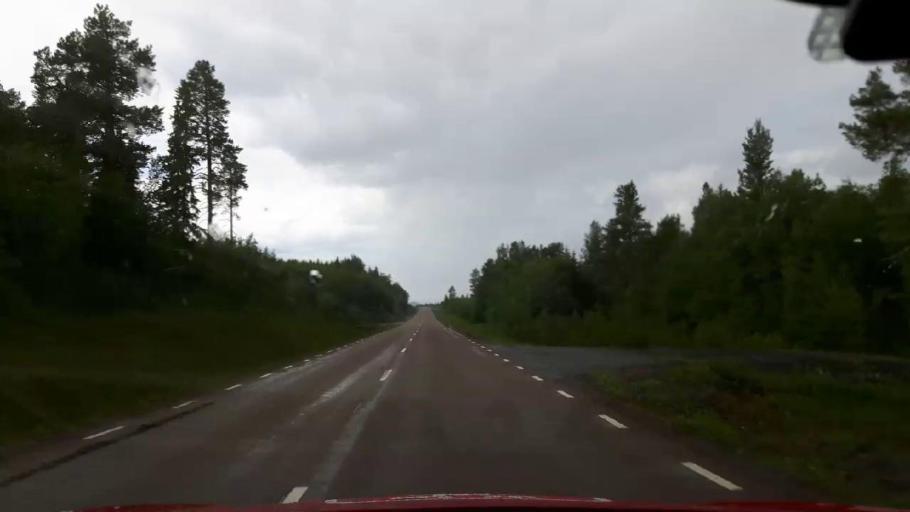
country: SE
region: Jaemtland
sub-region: Krokoms Kommun
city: Krokom
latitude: 63.8838
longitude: 14.2853
